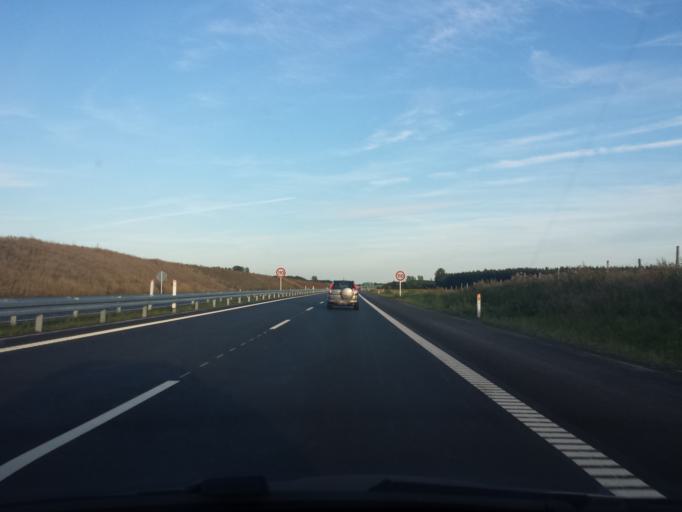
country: DK
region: Capital Region
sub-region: Ballerup Kommune
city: Ballerup
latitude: 55.7119
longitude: 12.3377
